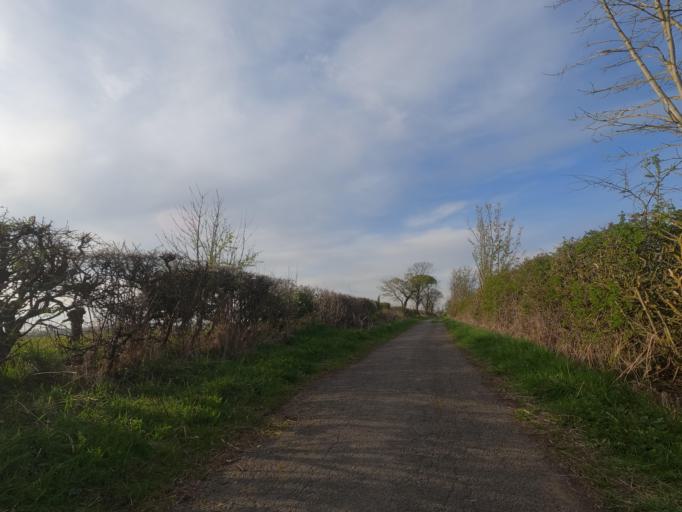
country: GB
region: England
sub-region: Northumberland
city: Cramlington
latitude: 55.0772
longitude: -1.6080
